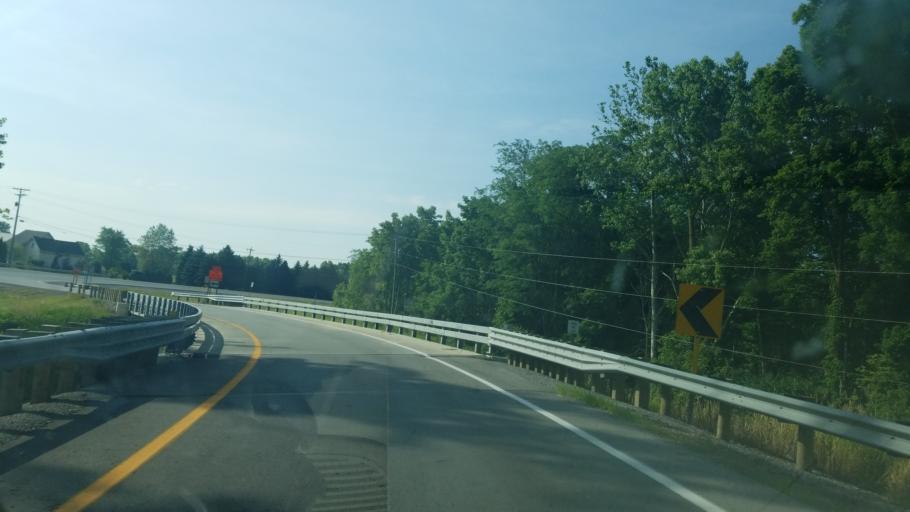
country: US
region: Ohio
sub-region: Hancock County
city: Findlay
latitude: 40.9890
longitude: -83.6518
